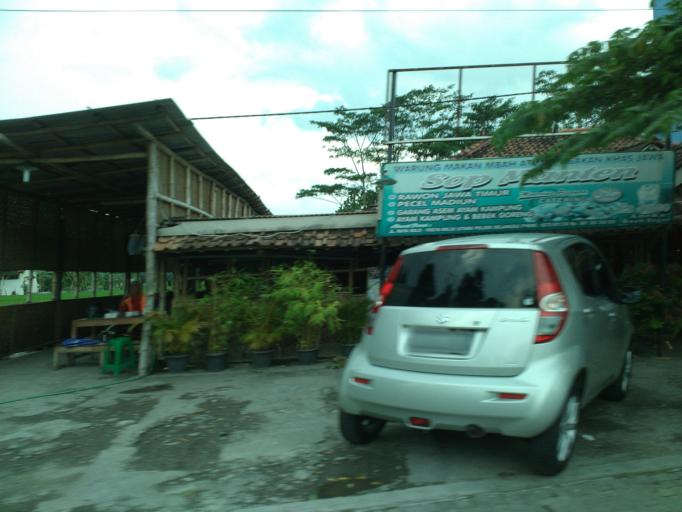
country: ID
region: Central Java
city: Delanggu
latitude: -7.6143
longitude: 110.7008
